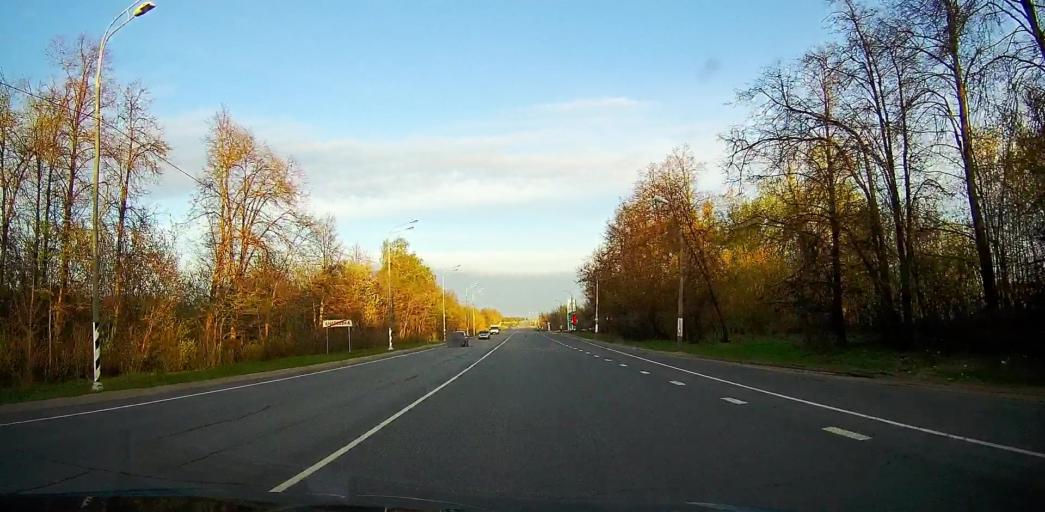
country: RU
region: Moskovskaya
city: Troitskoye
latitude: 55.2221
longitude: 38.5765
